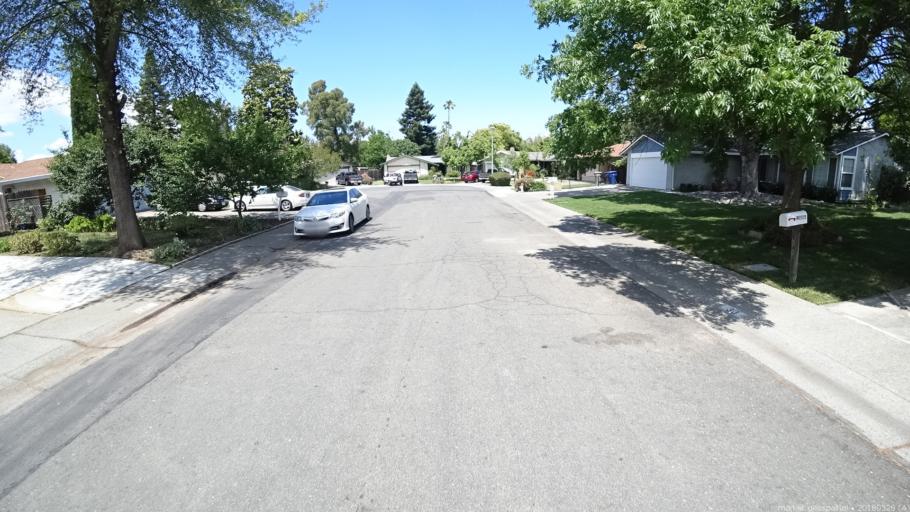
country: US
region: California
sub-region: Sacramento County
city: Sacramento
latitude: 38.6139
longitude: -121.5008
